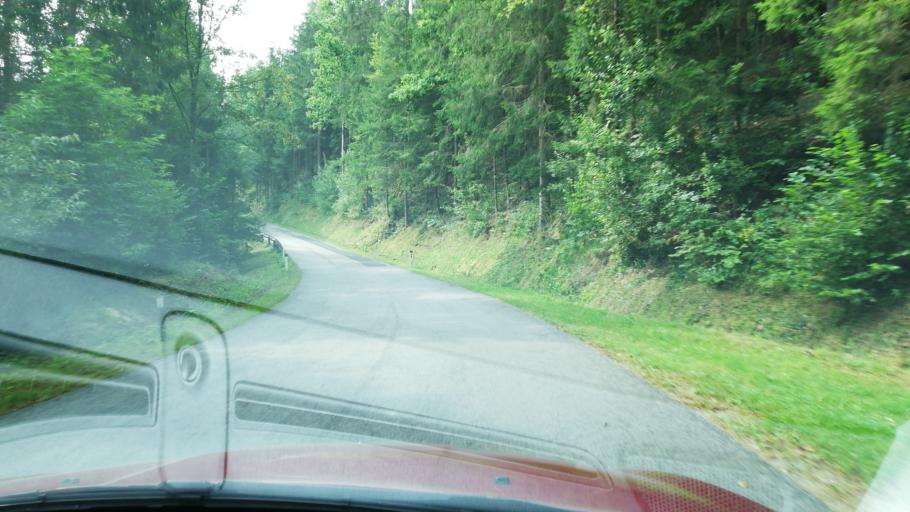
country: AT
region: Upper Austria
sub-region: Politischer Bezirk Rohrbach
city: Kleinzell im Muehlkreis
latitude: 48.5003
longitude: 14.0082
